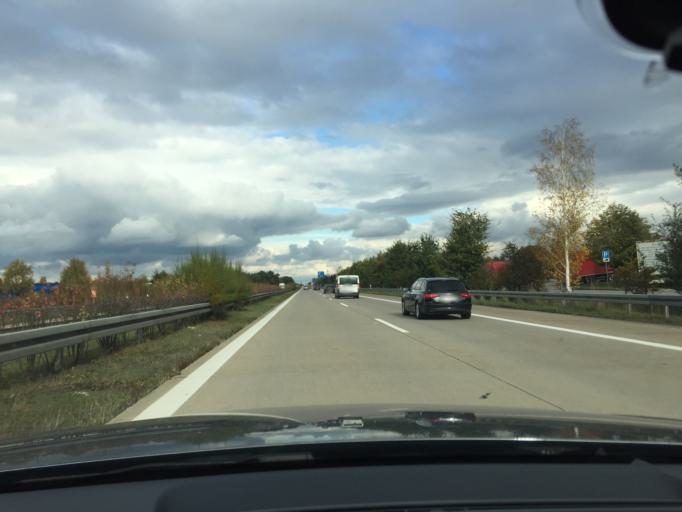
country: DE
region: Brandenburg
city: Ruhland
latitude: 51.4575
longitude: 13.8512
